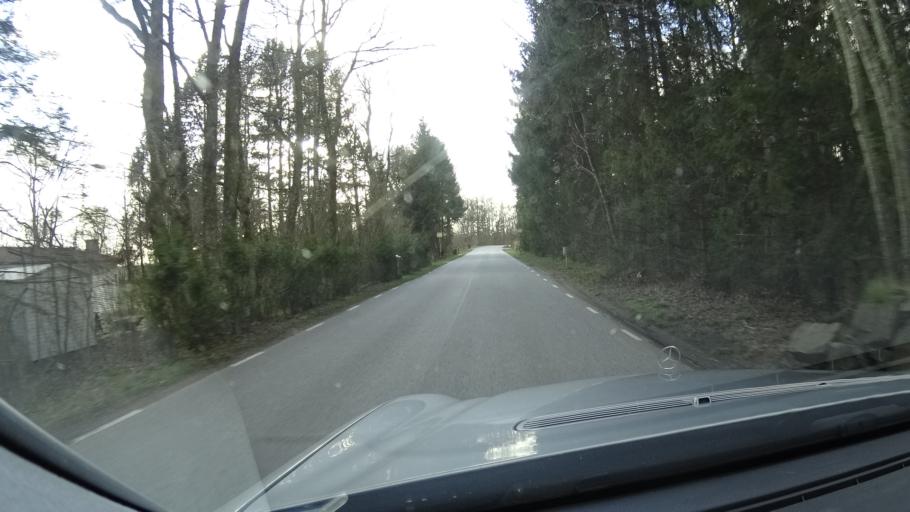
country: SE
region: Skane
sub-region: Hoors Kommun
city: Satofta
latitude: 55.9034
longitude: 13.5898
